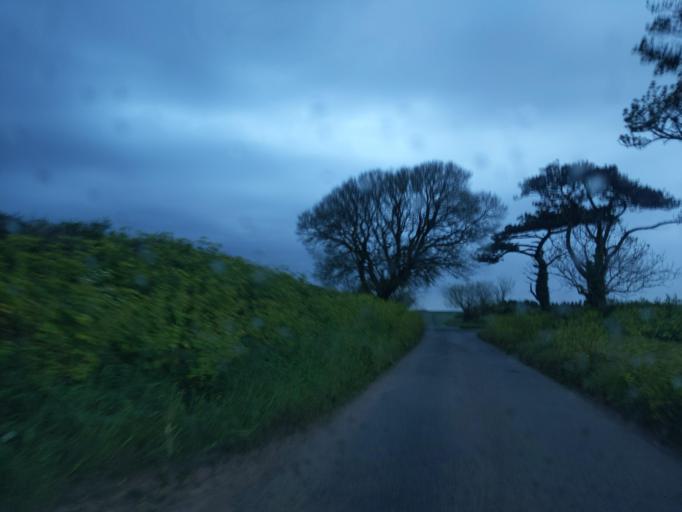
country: GB
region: England
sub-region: Devon
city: Dartmouth
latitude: 50.3603
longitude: -3.5477
